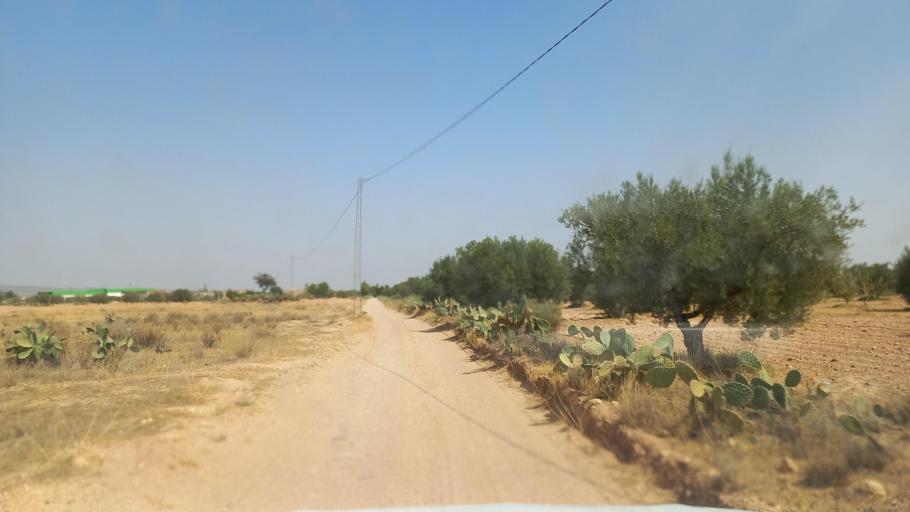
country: TN
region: Al Qasrayn
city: Kasserine
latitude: 35.2499
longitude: 9.0067
